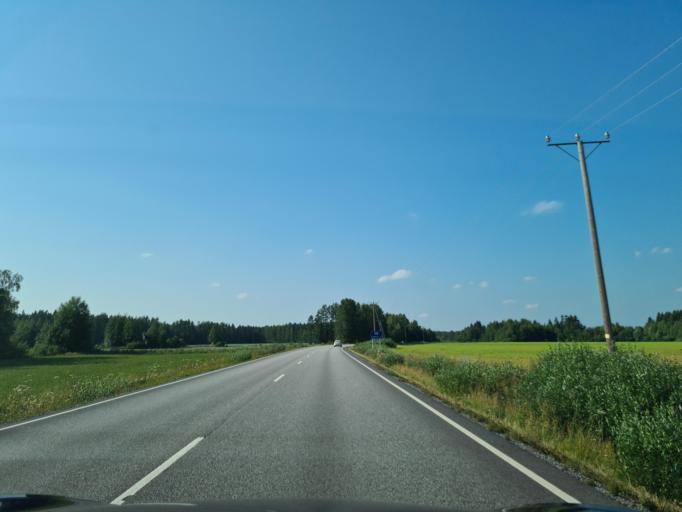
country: FI
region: Satakunta
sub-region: Pohjois-Satakunta
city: Karvia
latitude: 61.9623
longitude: 22.5101
